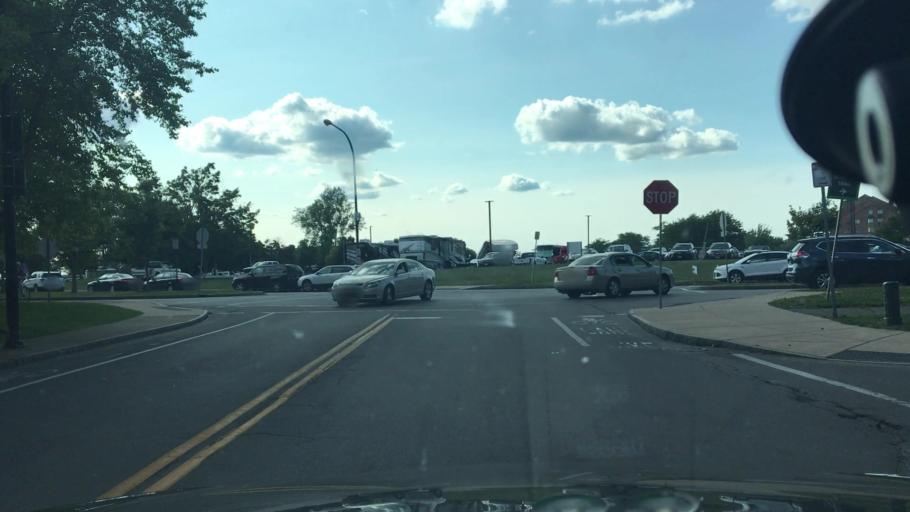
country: US
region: New York
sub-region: Erie County
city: Buffalo
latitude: 42.8788
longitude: -78.8819
